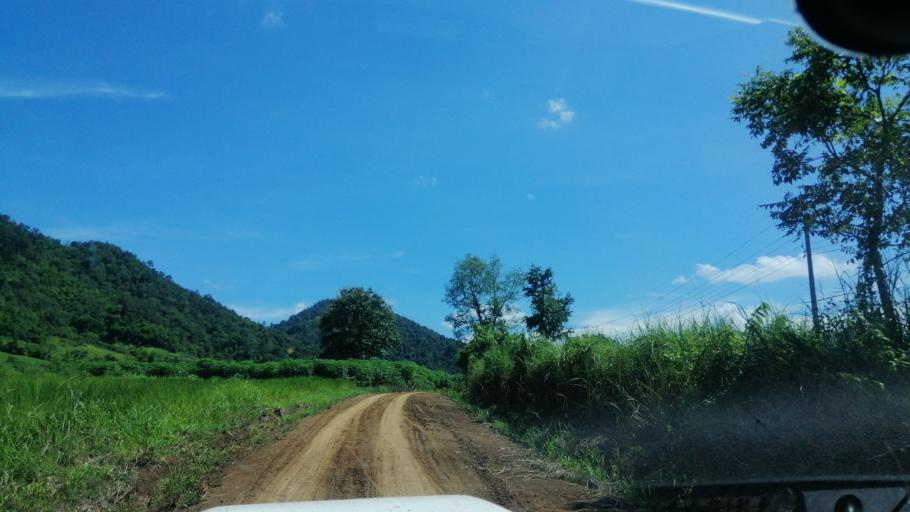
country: TH
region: Uttaradit
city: Ban Khok
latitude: 18.0870
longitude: 101.2433
